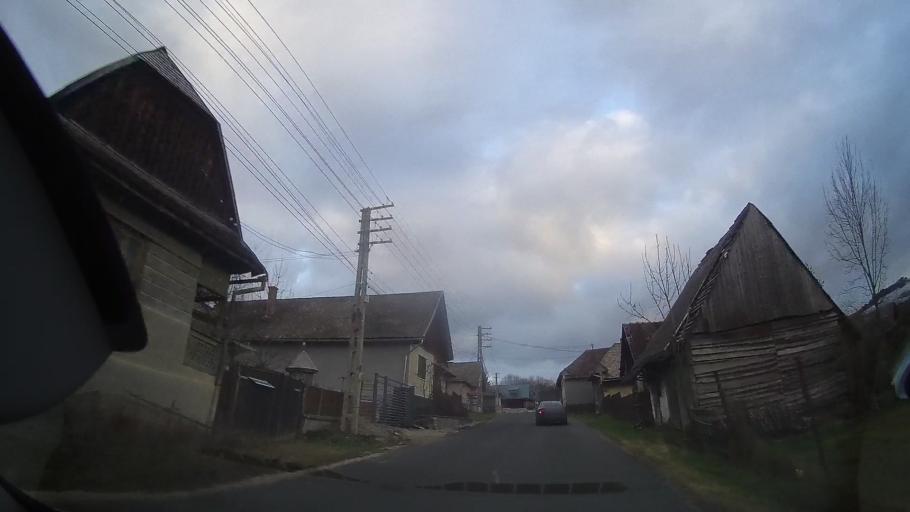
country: RO
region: Cluj
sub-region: Comuna Calatele
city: Calatele
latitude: 46.7820
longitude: 23.0288
